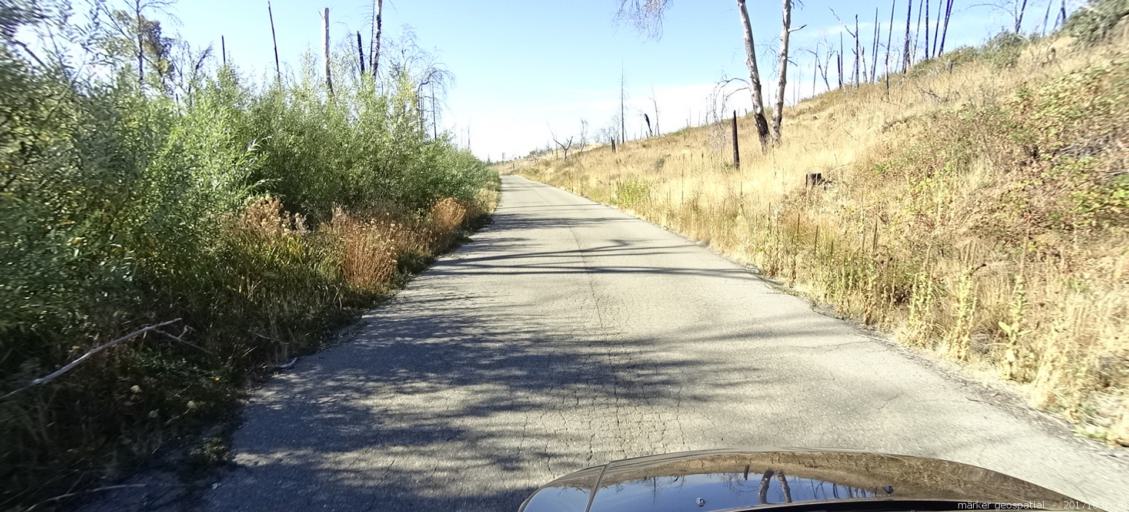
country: US
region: California
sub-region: Shasta County
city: Shingletown
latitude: 40.4550
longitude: -121.7949
